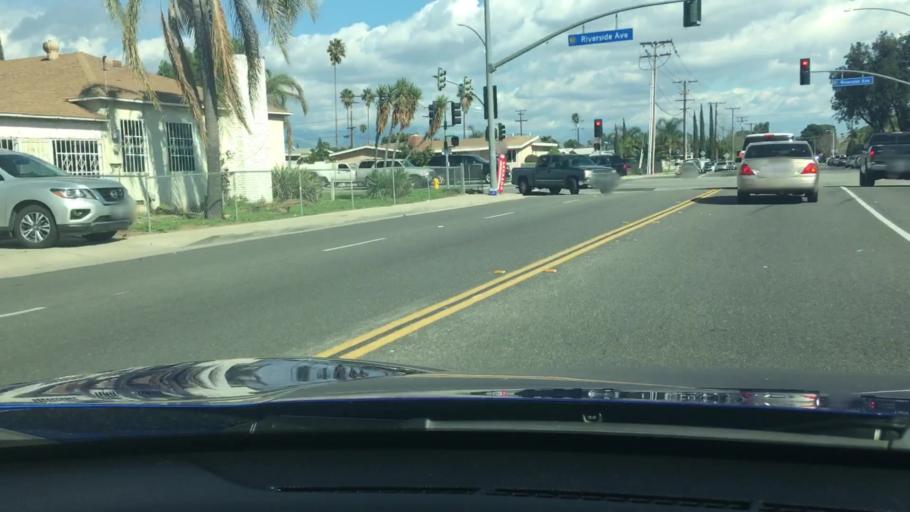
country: US
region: California
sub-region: San Bernardino County
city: Rialto
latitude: 34.0851
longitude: -117.3709
